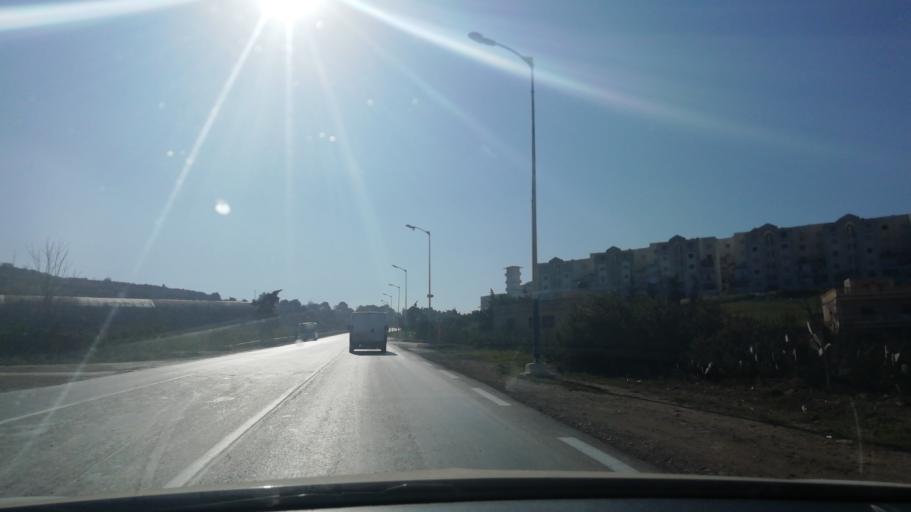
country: DZ
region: Tlemcen
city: Nedroma
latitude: 35.0987
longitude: -1.8338
